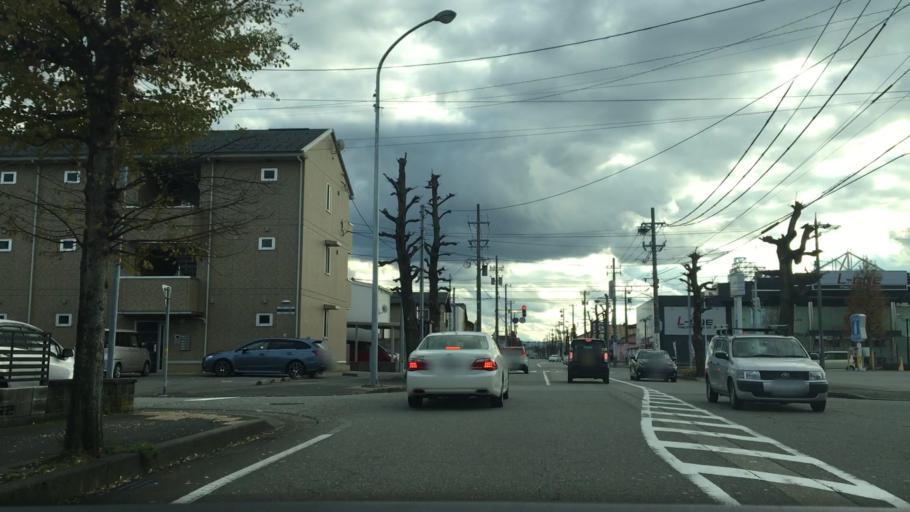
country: JP
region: Ishikawa
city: Nonoichi
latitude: 36.5221
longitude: 136.6174
